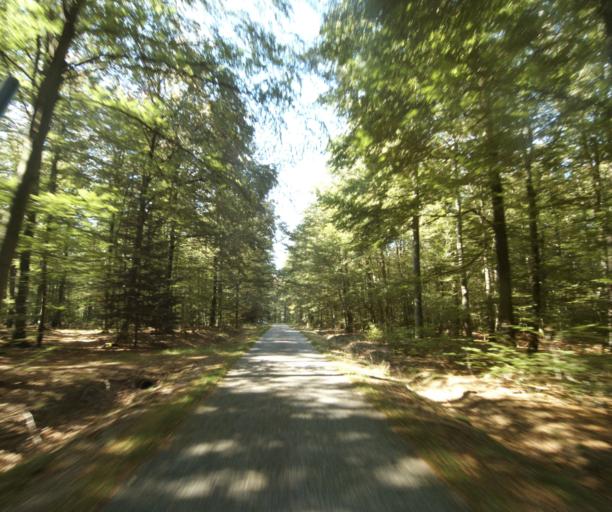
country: FR
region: Lorraine
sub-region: Departement des Vosges
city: Deyvillers
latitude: 48.1680
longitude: 6.5412
